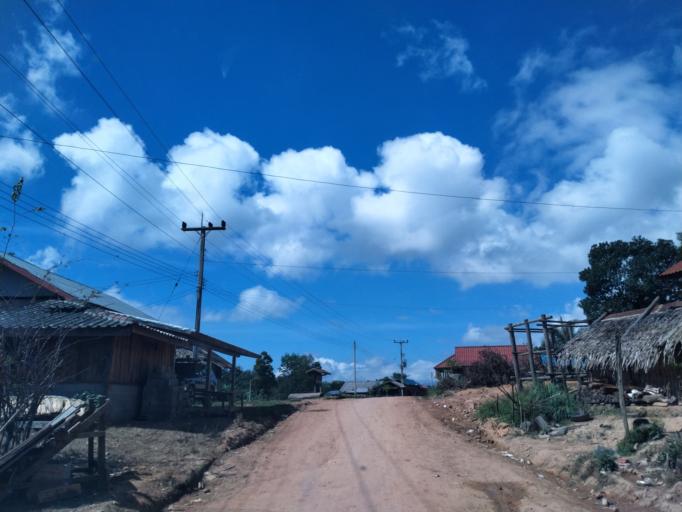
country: TH
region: Nong Khai
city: Rattanawapi
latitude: 18.6369
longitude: 102.9543
